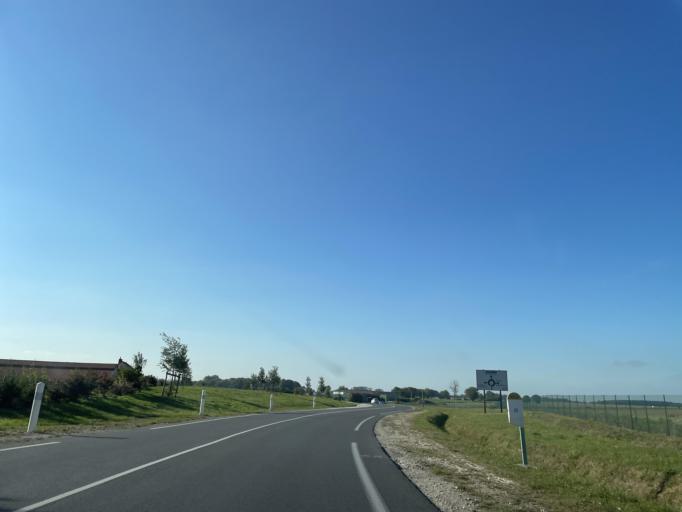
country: FR
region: Ile-de-France
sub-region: Departement de Seine-et-Marne
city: Pommeuse
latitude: 48.8354
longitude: 2.9907
